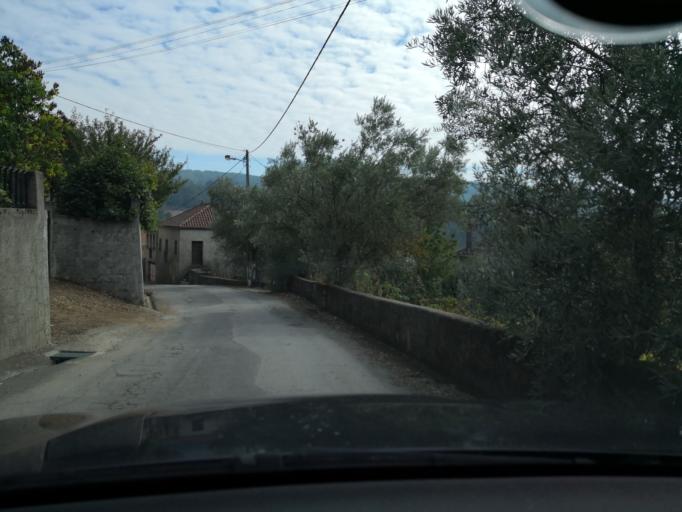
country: PT
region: Vila Real
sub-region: Sabrosa
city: Vilela
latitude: 41.2214
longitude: -7.6893
